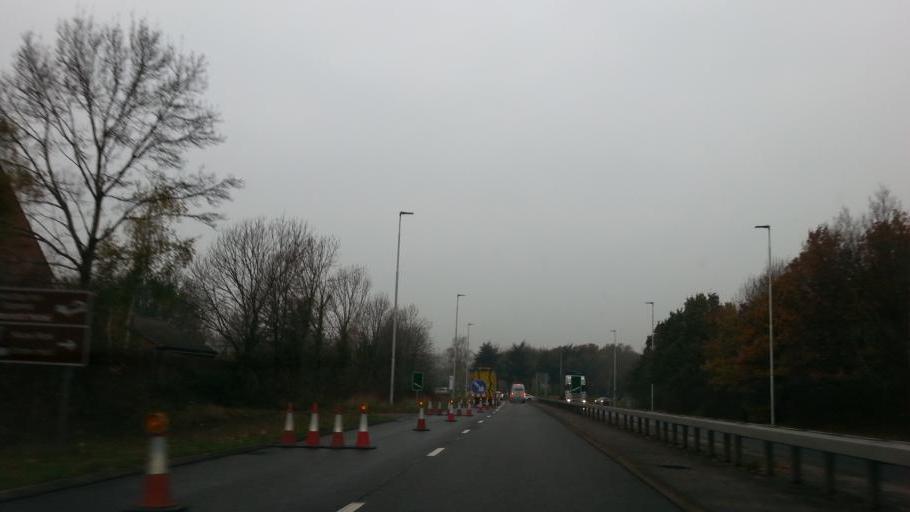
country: GB
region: England
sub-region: Peterborough
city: Castor
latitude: 52.5507
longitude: -0.3111
